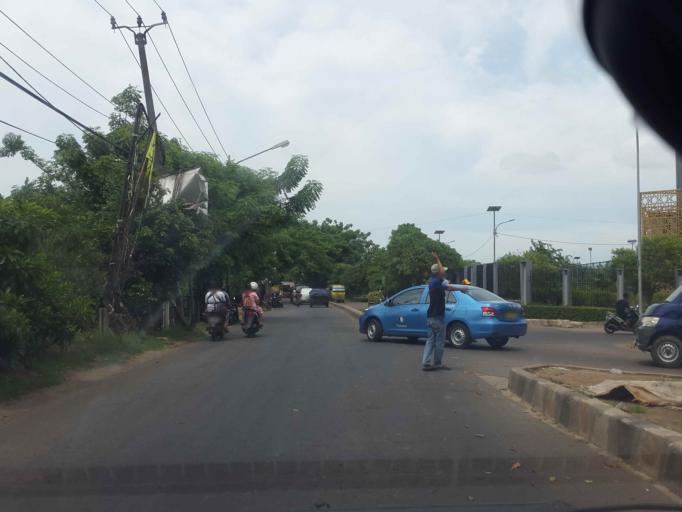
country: ID
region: Banten
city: Tangerang
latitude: -6.1550
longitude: 106.6418
